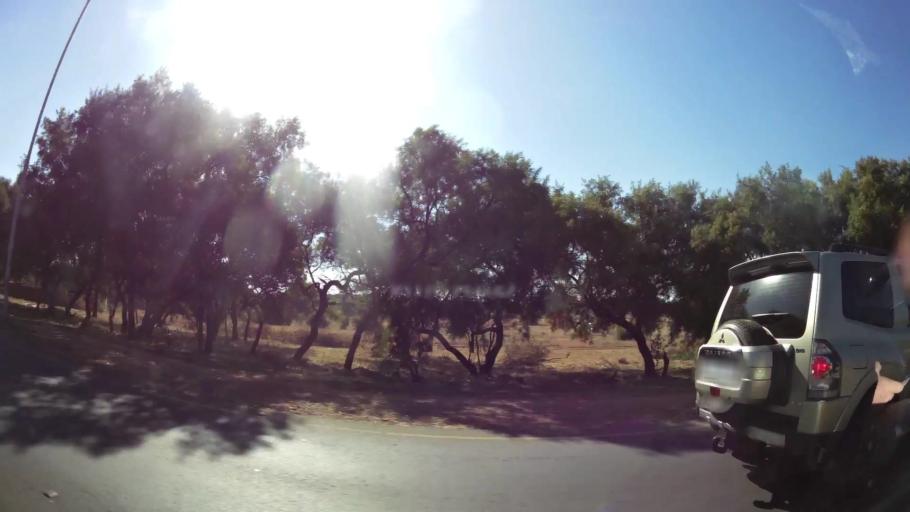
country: ZA
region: Gauteng
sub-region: City of Tshwane Metropolitan Municipality
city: Pretoria
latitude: -25.7334
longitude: 28.2329
